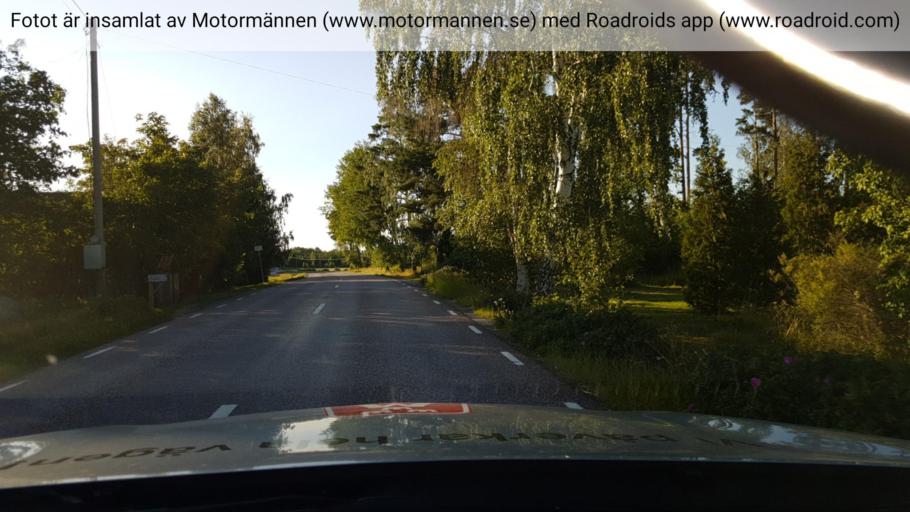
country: SE
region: Vaestmanland
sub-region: Surahammars Kommun
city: Ramnas
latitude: 59.9275
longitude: 16.3056
